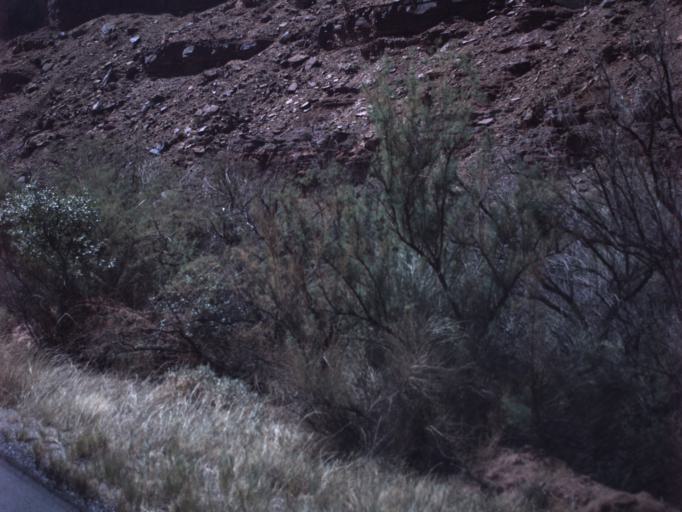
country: US
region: Utah
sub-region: Grand County
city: Moab
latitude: 38.6539
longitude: -109.5049
